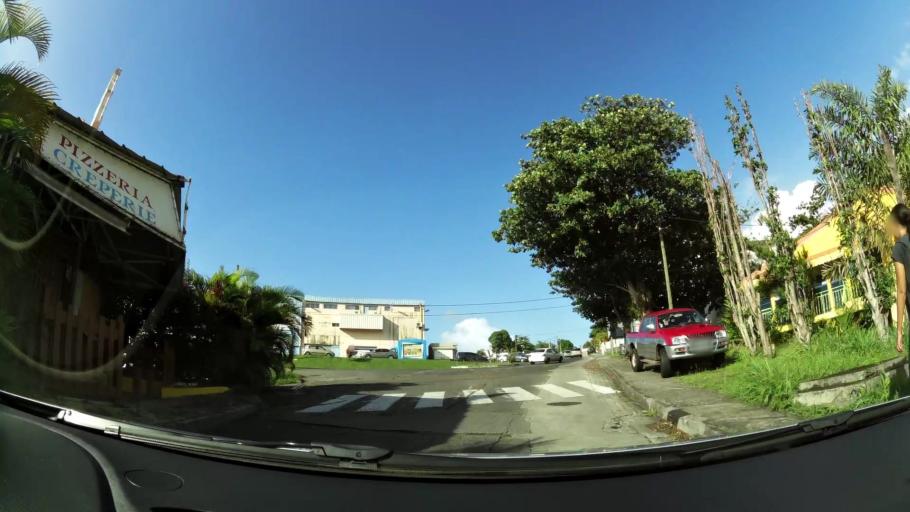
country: MQ
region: Martinique
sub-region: Martinique
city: Ducos
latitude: 14.5726
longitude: -60.9806
